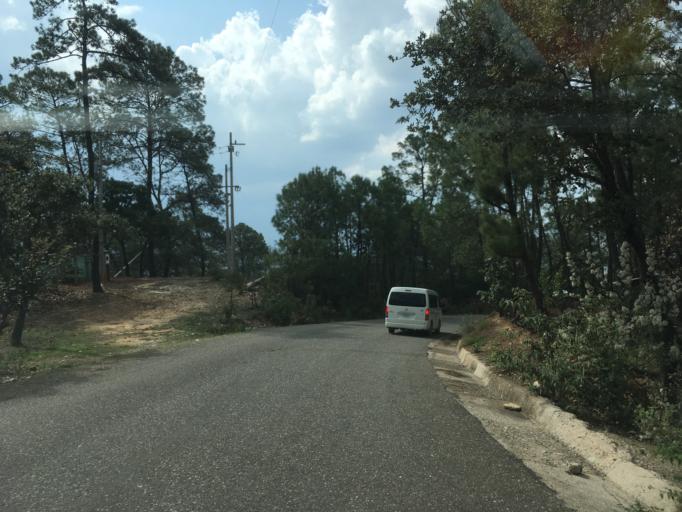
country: MX
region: Oaxaca
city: Santiago Tilantongo
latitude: 17.2108
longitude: -97.2806
